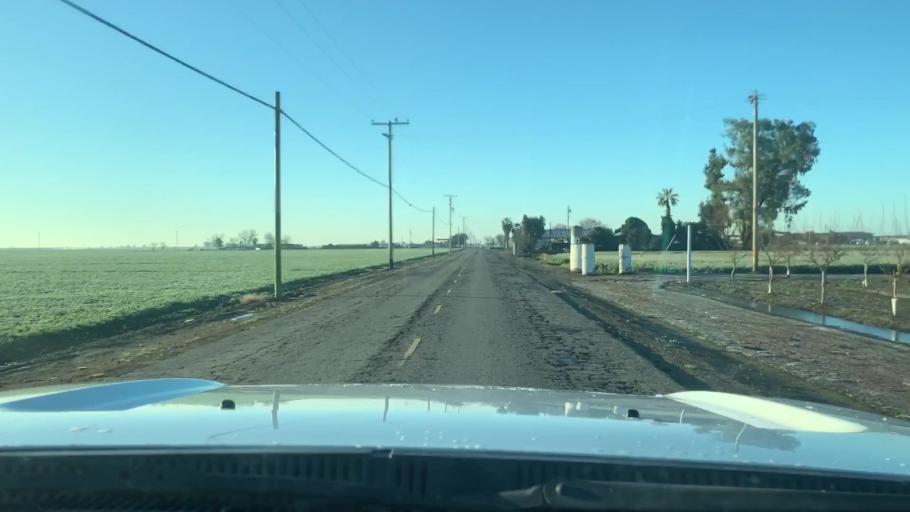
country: US
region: California
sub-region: Kings County
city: Corcoran
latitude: 36.2075
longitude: -119.4930
